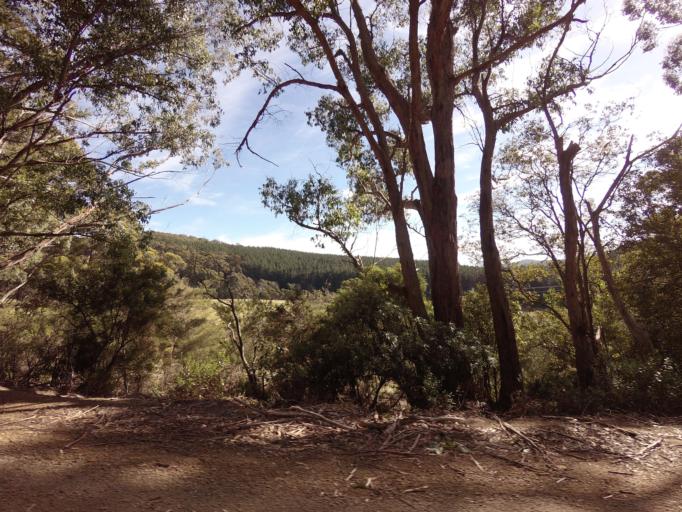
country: AU
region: Tasmania
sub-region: Clarence
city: Sandford
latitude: -43.1827
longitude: 147.7718
